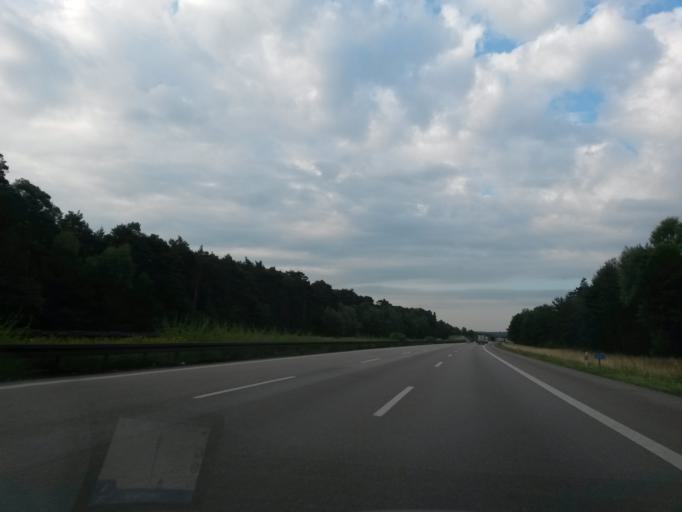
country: DE
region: Bavaria
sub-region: Upper Bavaria
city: Reichertshofen
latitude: 48.6655
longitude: 11.5099
